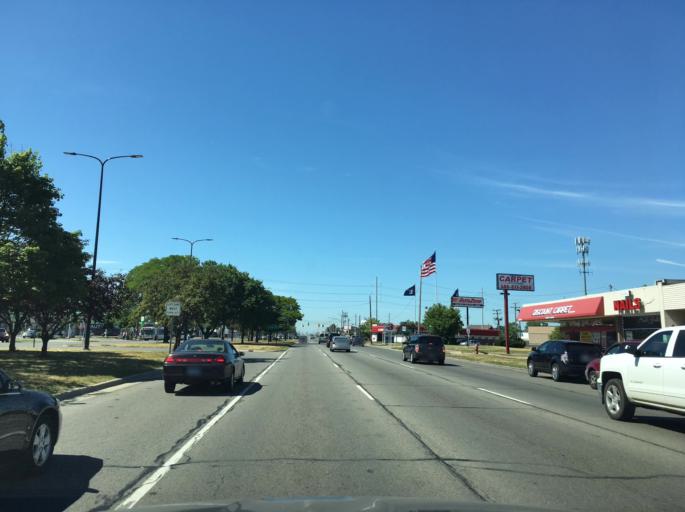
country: US
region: Michigan
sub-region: Macomb County
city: Eastpointe
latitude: 42.4519
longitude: -82.9666
